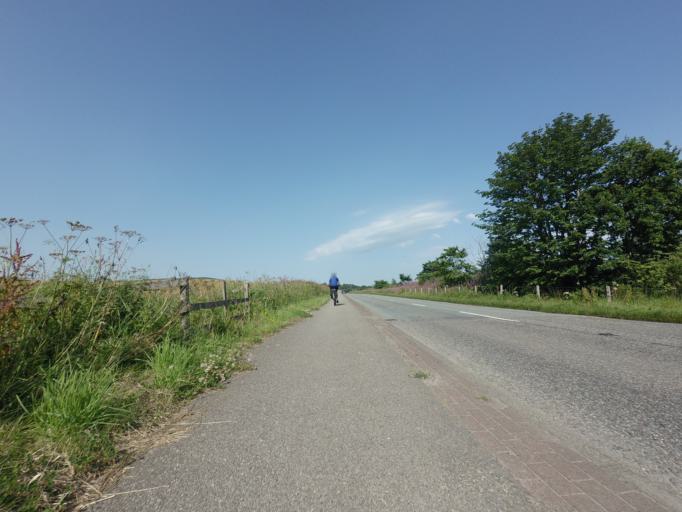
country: GB
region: Scotland
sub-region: Highland
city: Alness
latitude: 57.6845
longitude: -4.2894
